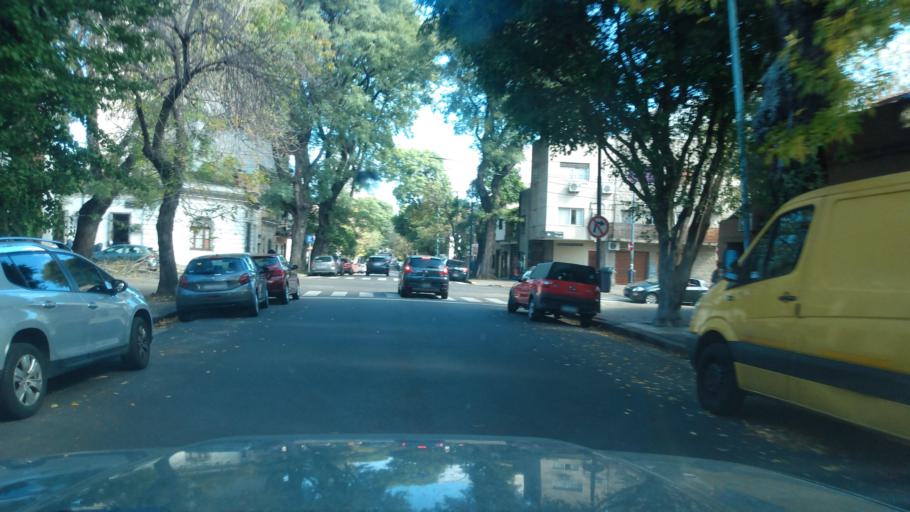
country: AR
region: Buenos Aires
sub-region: Partido de General San Martin
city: General San Martin
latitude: -34.5736
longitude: -58.4930
